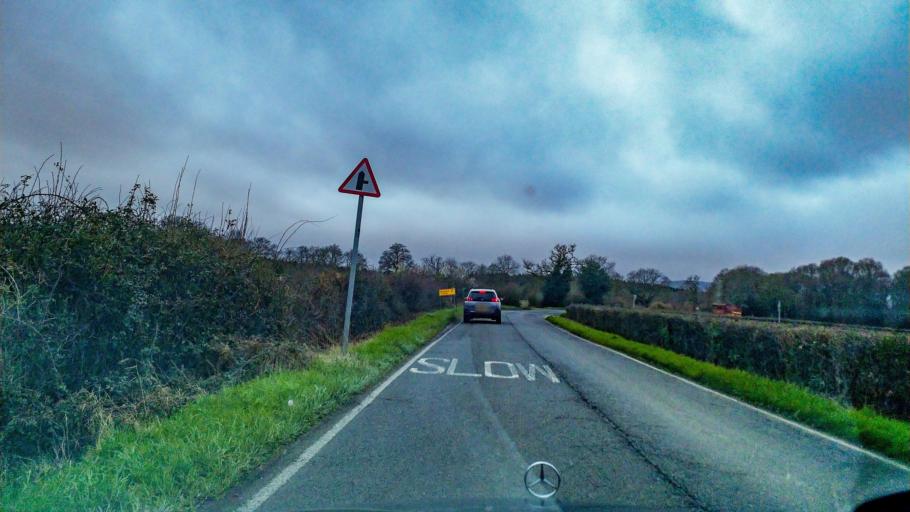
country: GB
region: England
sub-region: Surrey
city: Newdigate
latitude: 51.2067
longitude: -0.2930
